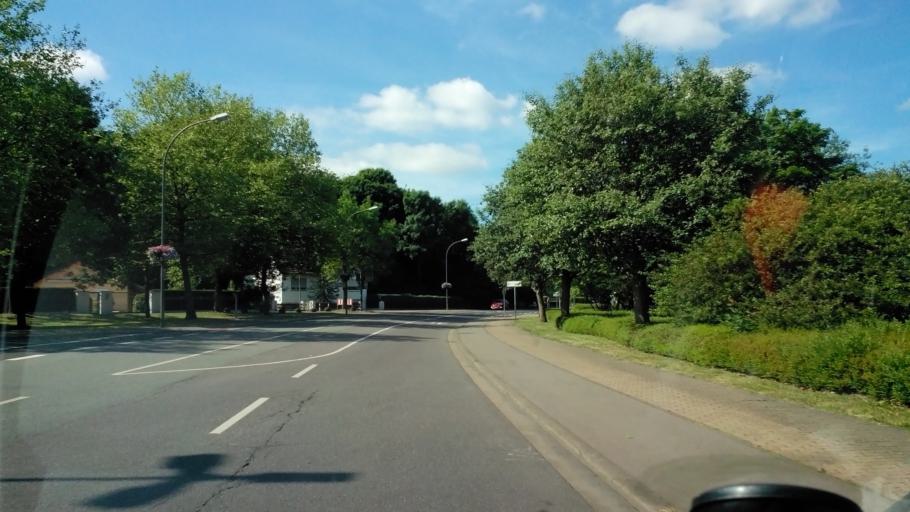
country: DE
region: Saarland
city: Saarlouis
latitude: 49.3220
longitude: 6.7435
